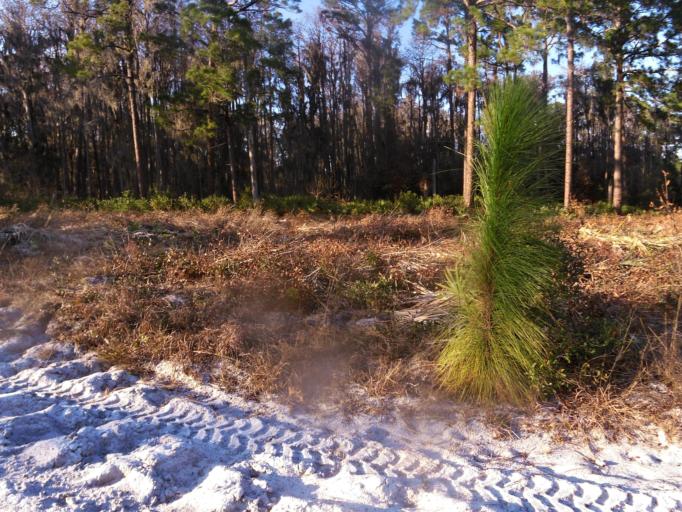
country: US
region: Florida
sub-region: Duval County
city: Atlantic Beach
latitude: 30.4776
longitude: -81.5044
